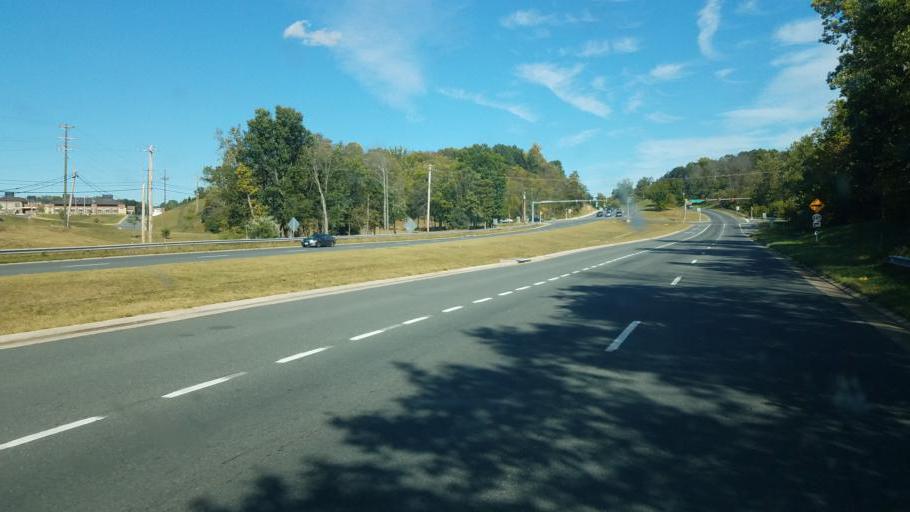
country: US
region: Virginia
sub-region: Warren County
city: Front Royal
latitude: 38.9043
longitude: -78.2076
